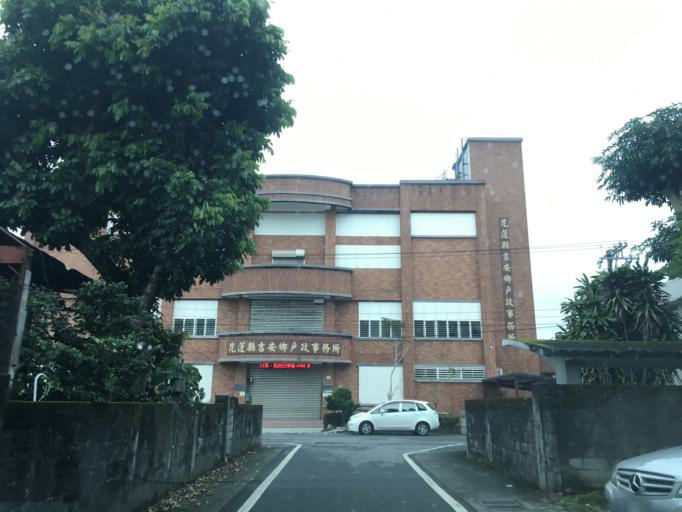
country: TW
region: Taiwan
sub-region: Hualien
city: Hualian
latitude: 23.9735
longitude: 121.5640
